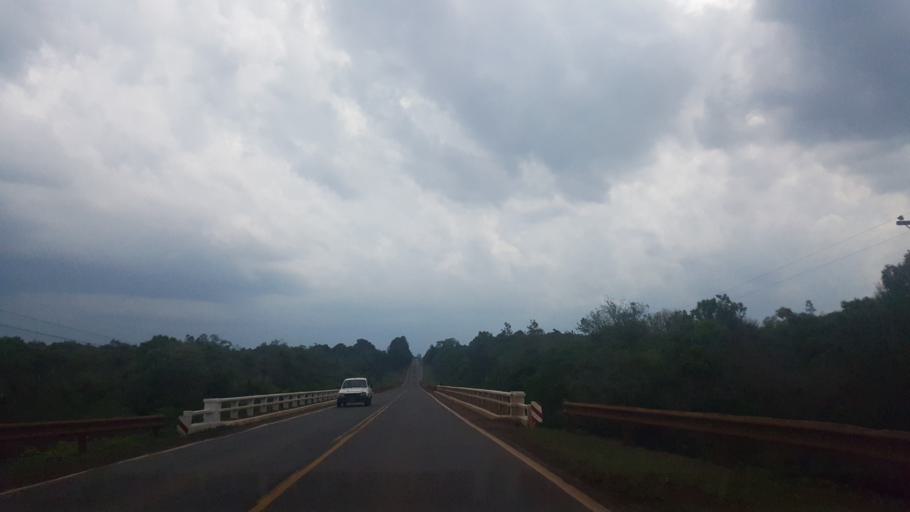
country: AR
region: Misiones
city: Santo Pipo
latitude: -27.1203
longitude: -55.3729
